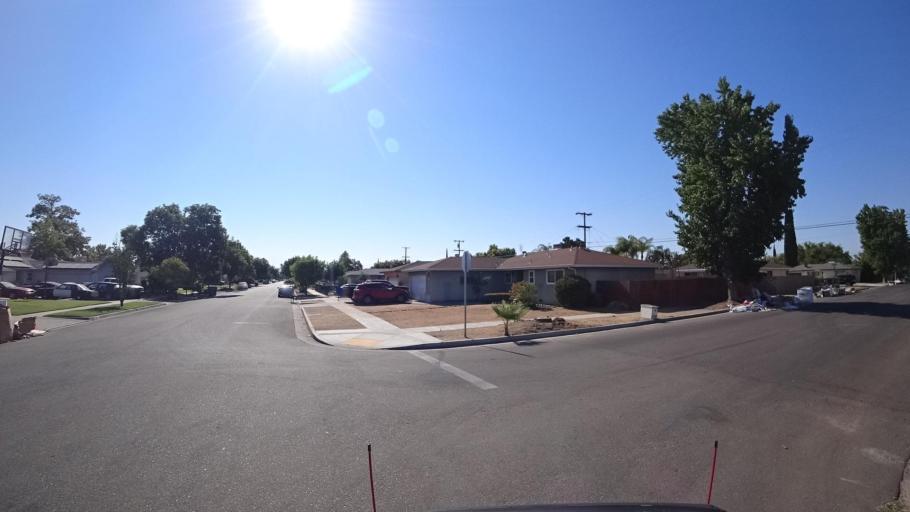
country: US
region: California
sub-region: Fresno County
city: Fresno
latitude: 36.7923
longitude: -119.7589
